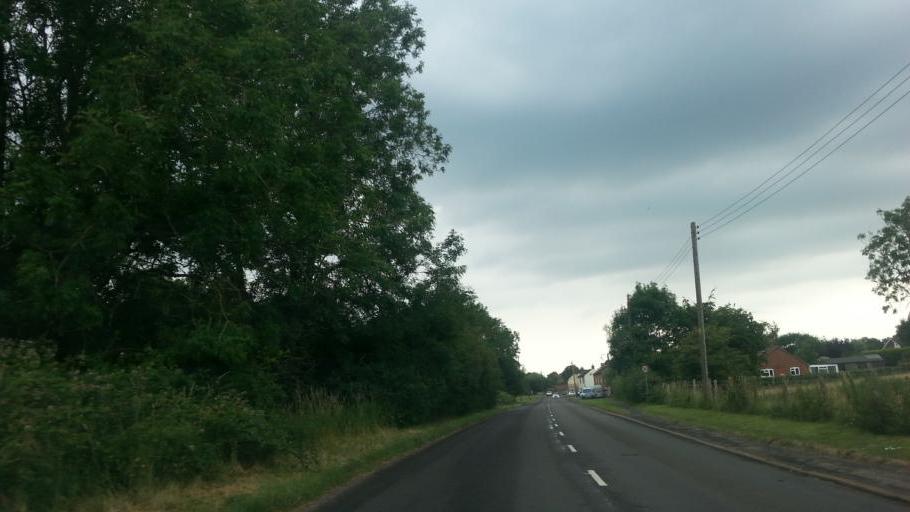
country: GB
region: England
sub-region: Norfolk
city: Fakenham
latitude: 52.8189
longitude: 0.6993
